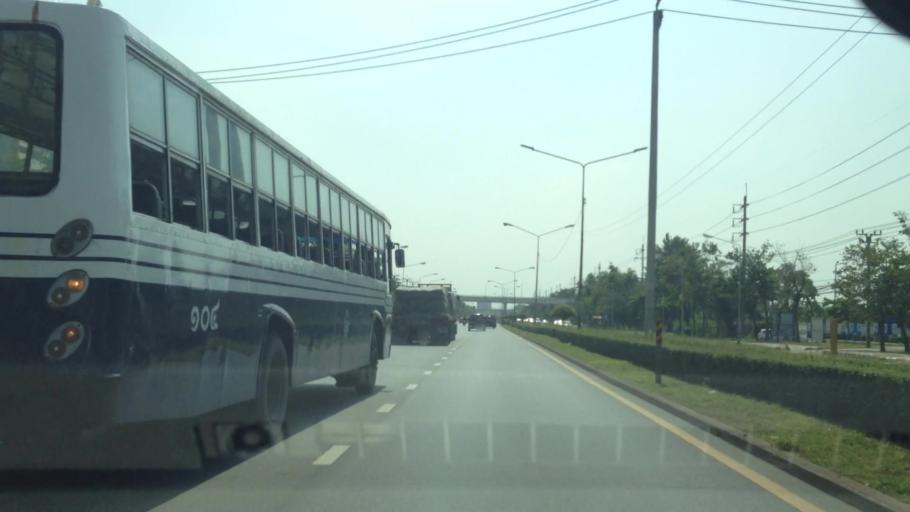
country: TH
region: Bangkok
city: Sai Mai
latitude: 13.9422
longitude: 100.6238
